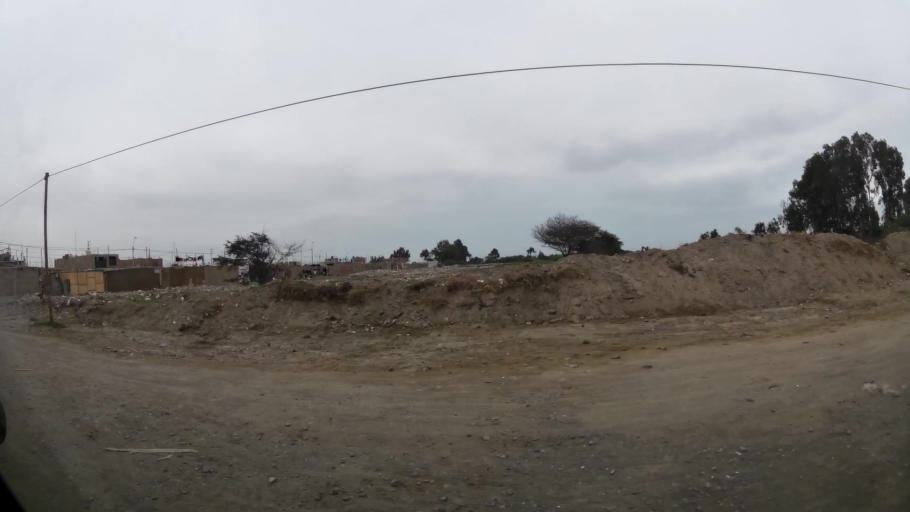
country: PE
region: Ica
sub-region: Provincia de Pisco
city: Pisco
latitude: -13.7300
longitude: -76.2011
